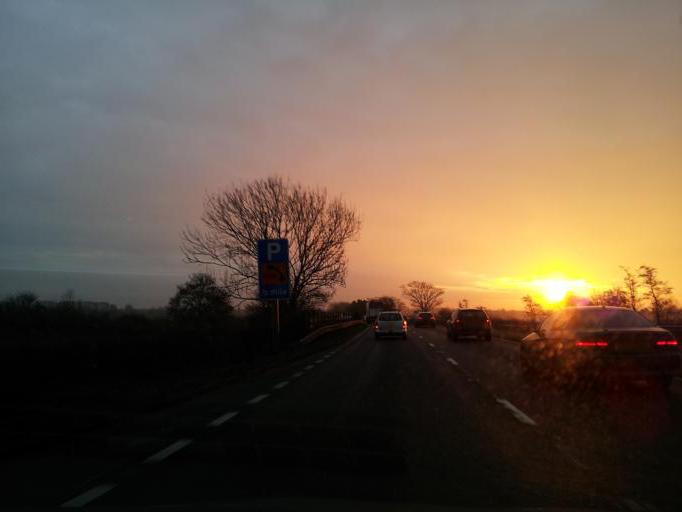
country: GB
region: England
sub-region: Peterborough
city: Castor
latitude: 52.5583
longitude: -0.3550
